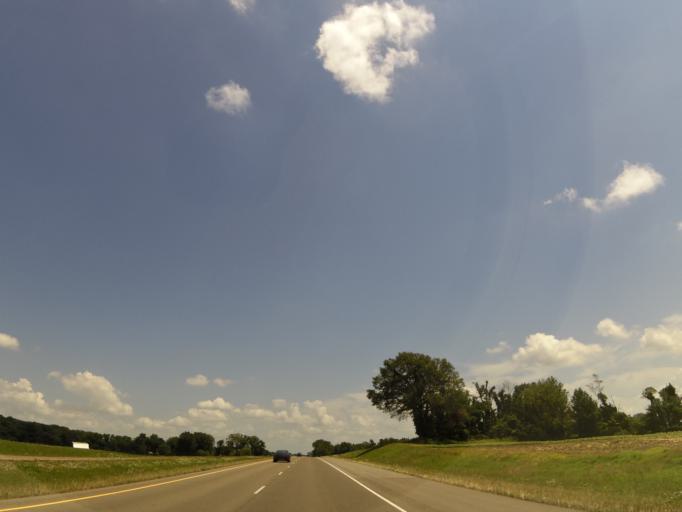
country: US
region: Tennessee
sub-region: Crockett County
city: Alamo
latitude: 35.8721
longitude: -89.2172
